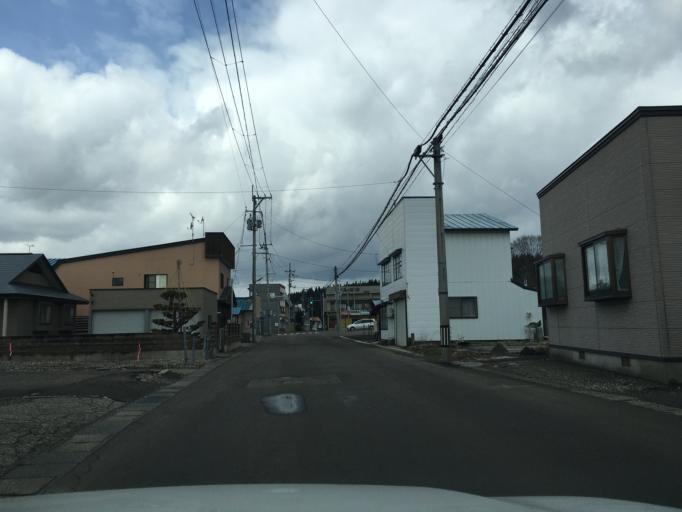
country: JP
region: Akita
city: Takanosu
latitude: 40.1603
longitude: 140.3309
